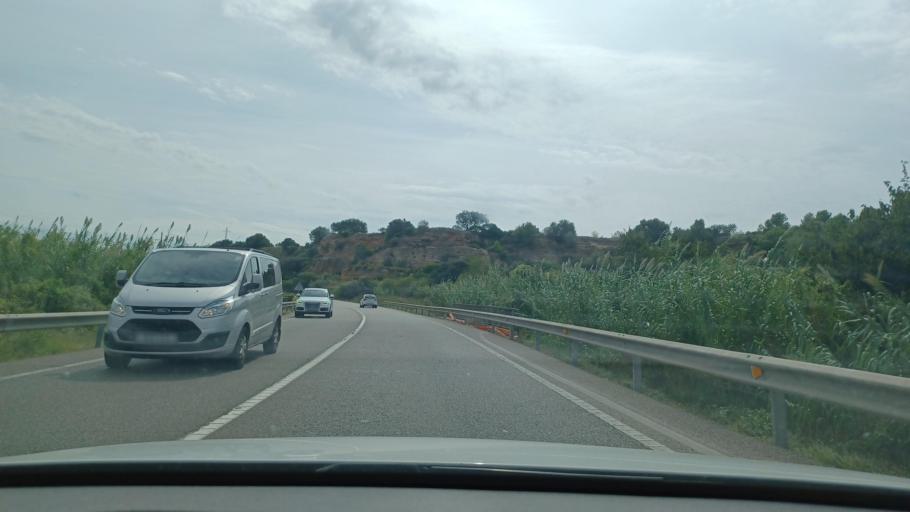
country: ES
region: Catalonia
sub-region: Provincia de Tarragona
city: Tortosa
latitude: 40.7888
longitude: 0.4965
